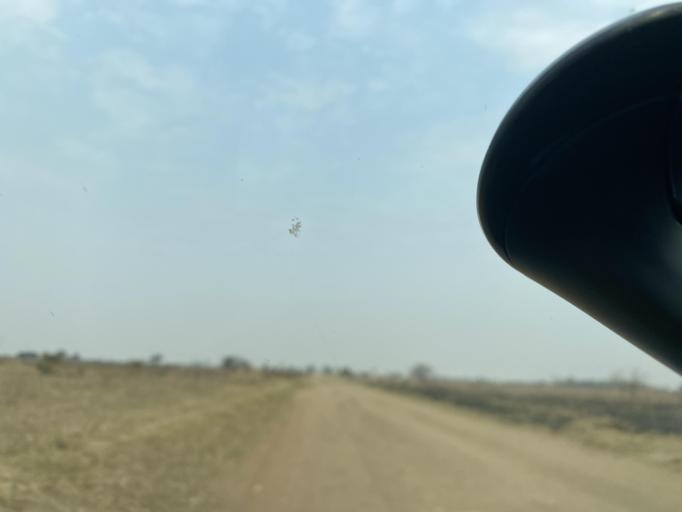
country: ZM
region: Lusaka
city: Kafue
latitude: -15.6442
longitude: 28.0846
